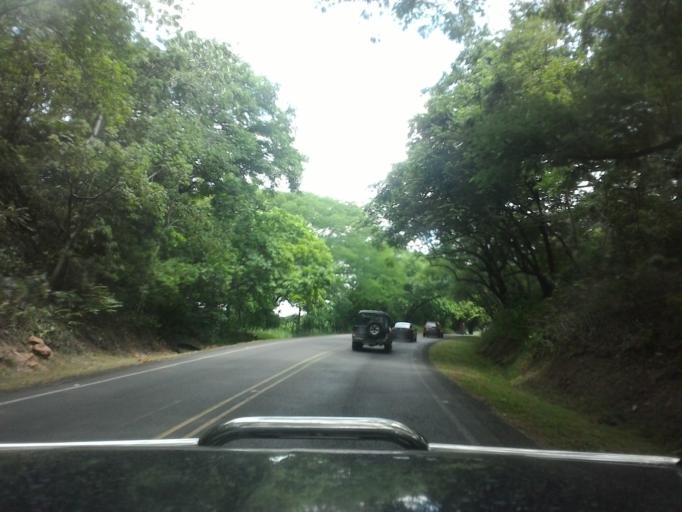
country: CR
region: Puntarenas
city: Miramar
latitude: 10.0836
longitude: -84.7871
